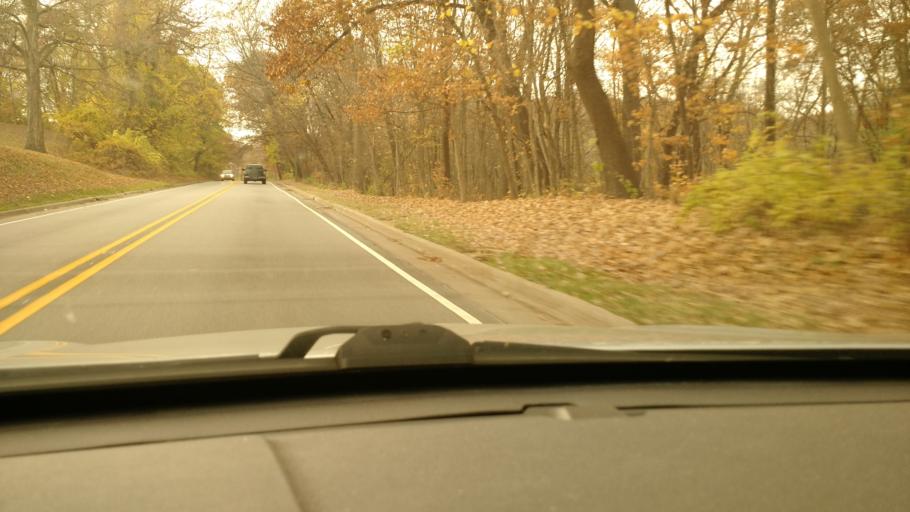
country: US
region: Illinois
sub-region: Rock Island County
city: Milan
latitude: 41.4649
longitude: -90.5692
